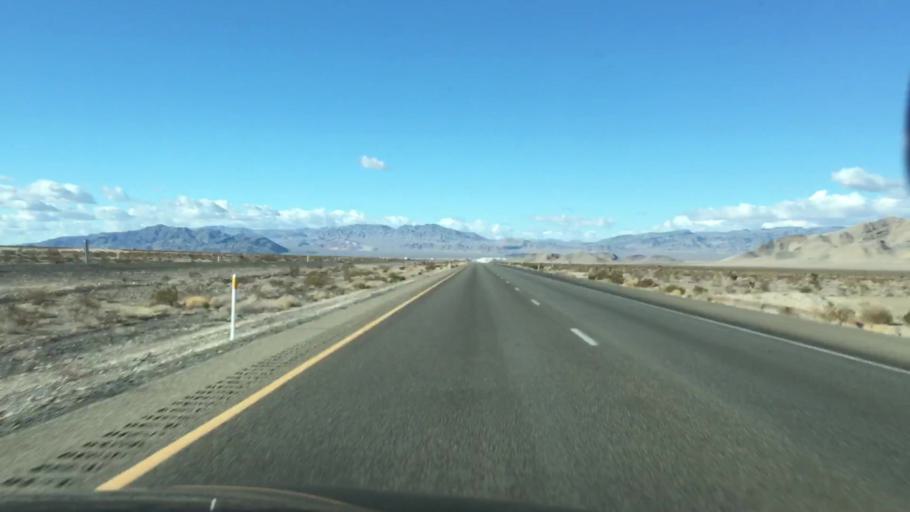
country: US
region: Nevada
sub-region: Nye County
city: Pahrump
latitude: 36.5606
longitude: -115.6117
